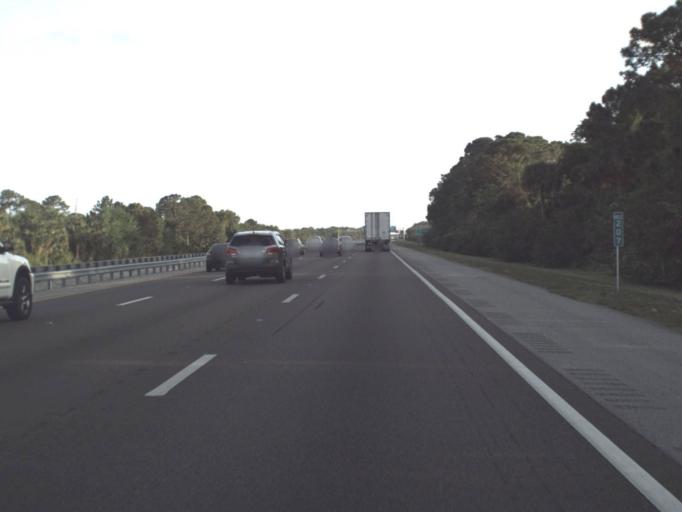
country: US
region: Florida
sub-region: Brevard County
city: Port Saint John
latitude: 28.4389
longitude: -80.8207
